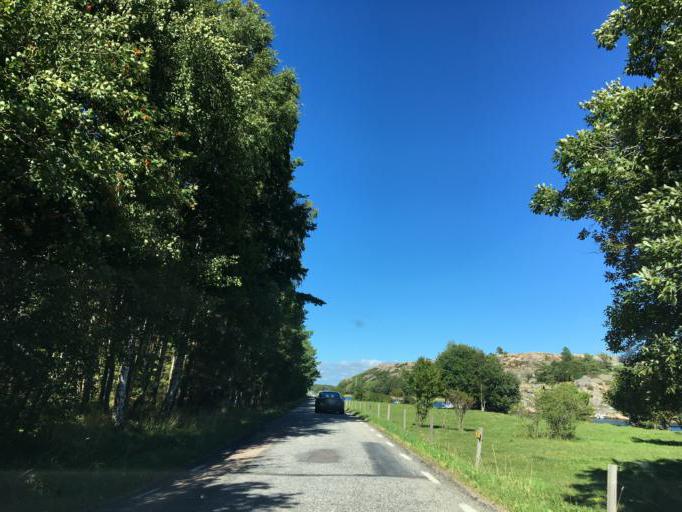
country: SE
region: Vaestra Goetaland
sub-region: Sotenas Kommun
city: Hunnebostrand
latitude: 58.4142
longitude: 11.2651
